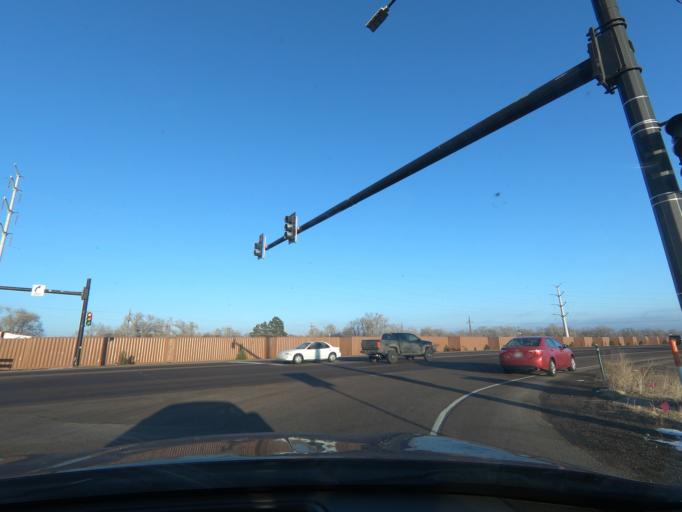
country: US
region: Colorado
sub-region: El Paso County
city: Stratmoor
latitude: 38.7668
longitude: -104.7597
